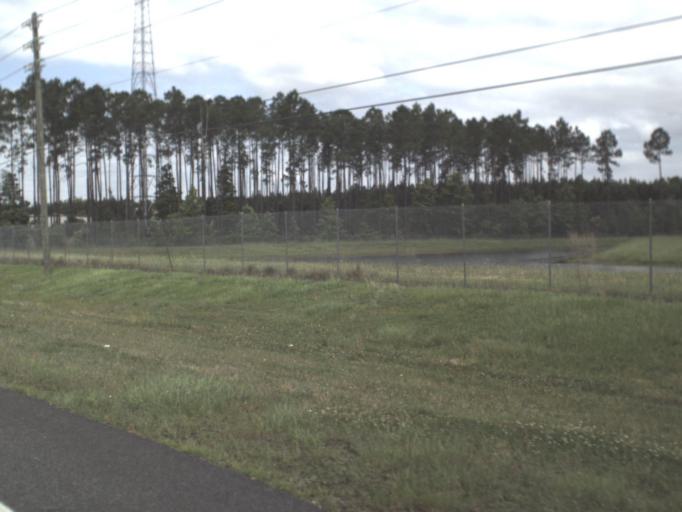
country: US
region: Florida
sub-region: Nassau County
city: Callahan
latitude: 30.6115
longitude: -81.7339
